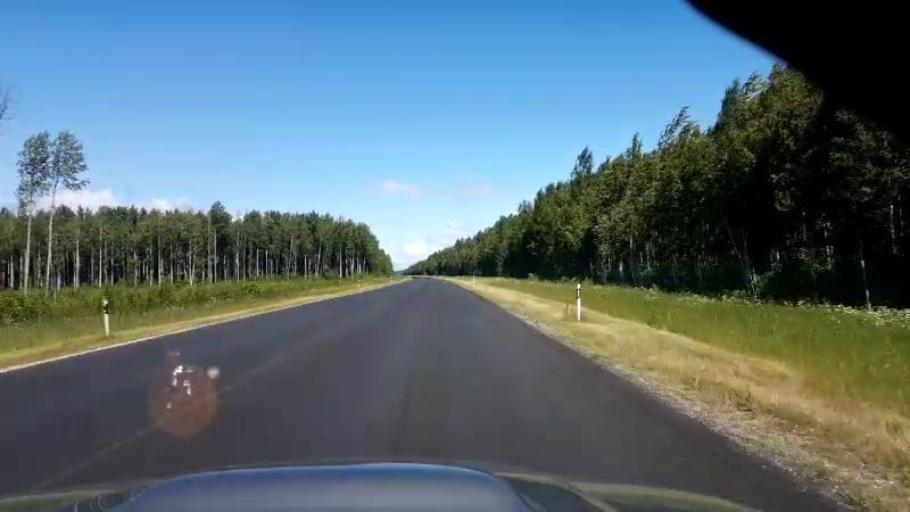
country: LV
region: Salacgrivas
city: Ainazi
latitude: 57.9140
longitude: 24.4200
